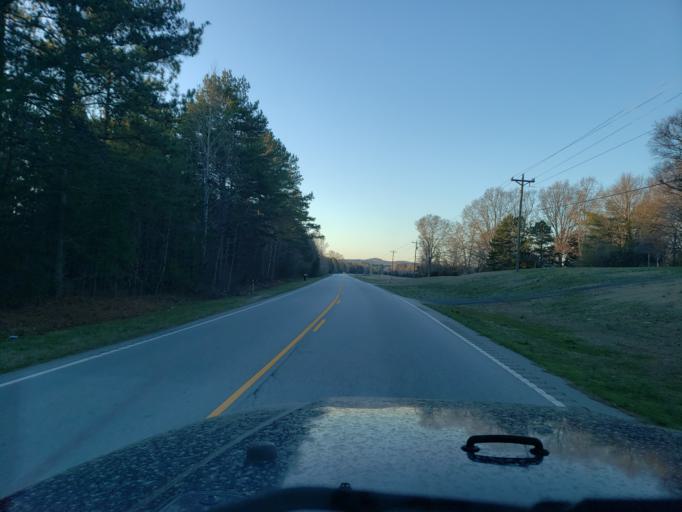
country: US
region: South Carolina
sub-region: York County
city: Clover
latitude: 35.1425
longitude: -81.3145
